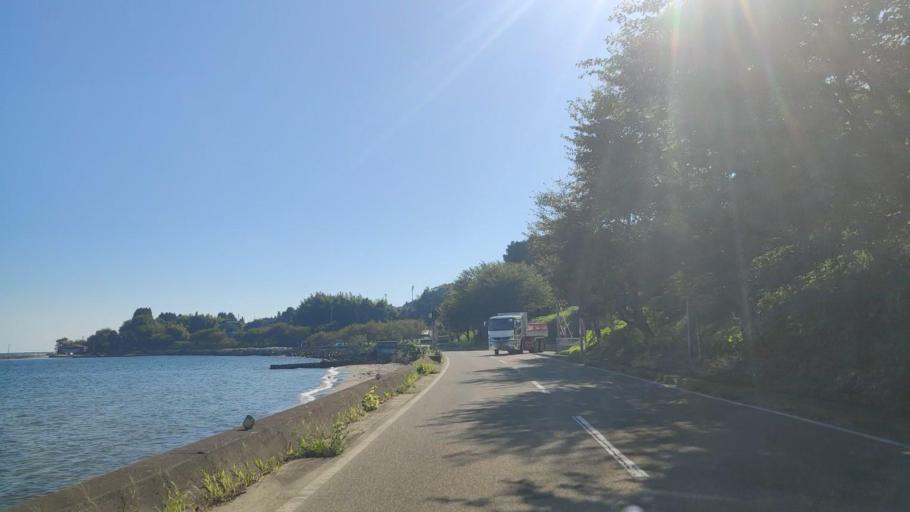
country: JP
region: Ishikawa
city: Nanao
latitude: 37.2785
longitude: 137.0981
